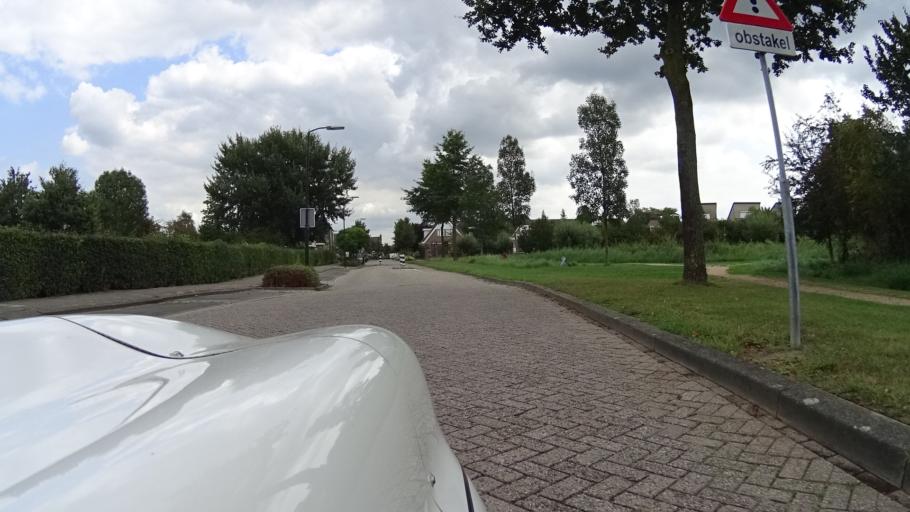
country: NL
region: South Holland
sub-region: Gemeente Hardinxveld-Giessendam
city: Neder-Hardinxveld
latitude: 51.8292
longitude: 4.8221
